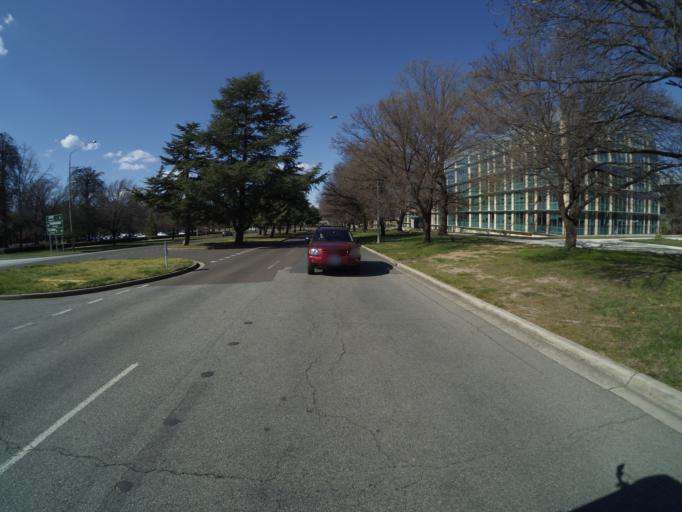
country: AU
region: Australian Capital Territory
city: Forrest
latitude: -35.3058
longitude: 149.1310
